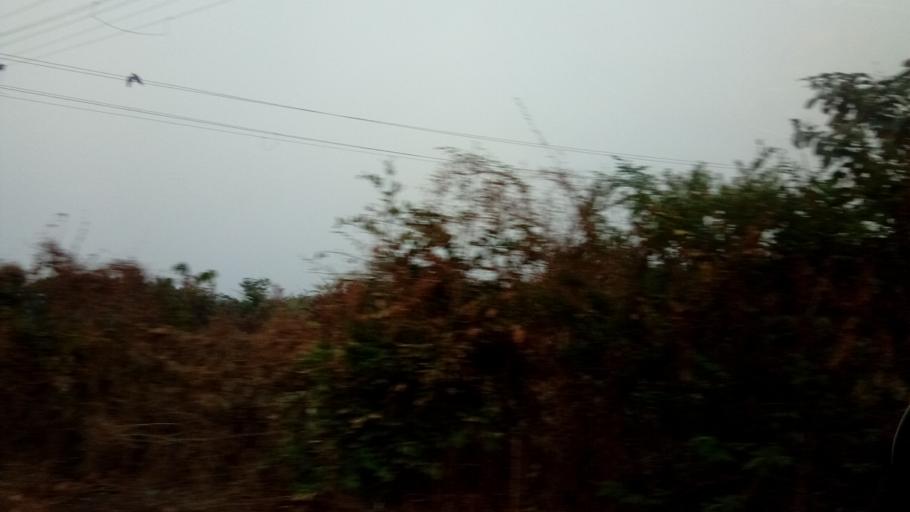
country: IN
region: Goa
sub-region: South Goa
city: Cavelossim
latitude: 15.1003
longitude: 73.9349
